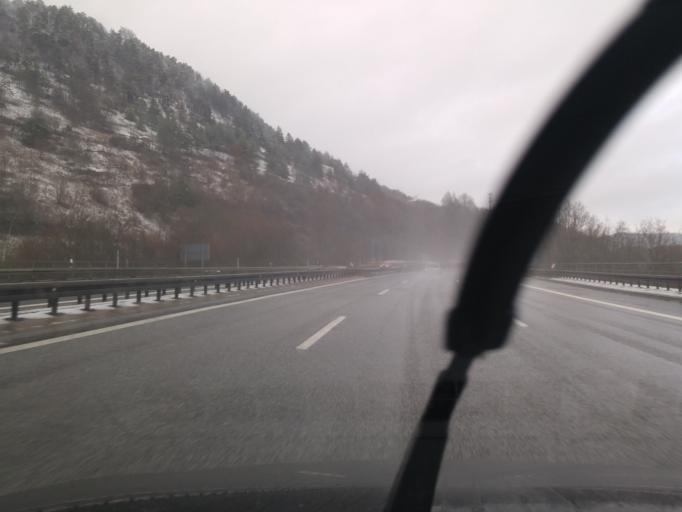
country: DE
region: Bavaria
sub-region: Regierungsbezirk Unterfranken
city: Elfershausen
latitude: 50.1456
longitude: 9.9509
